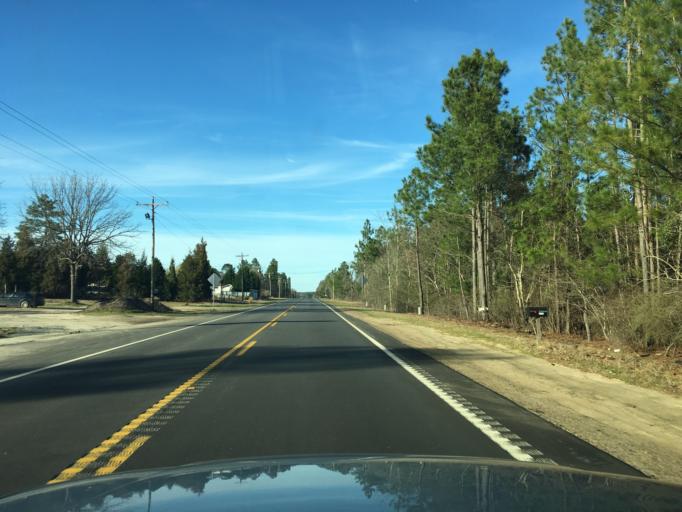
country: US
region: South Carolina
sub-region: Aiken County
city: Aiken
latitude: 33.7143
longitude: -81.6581
